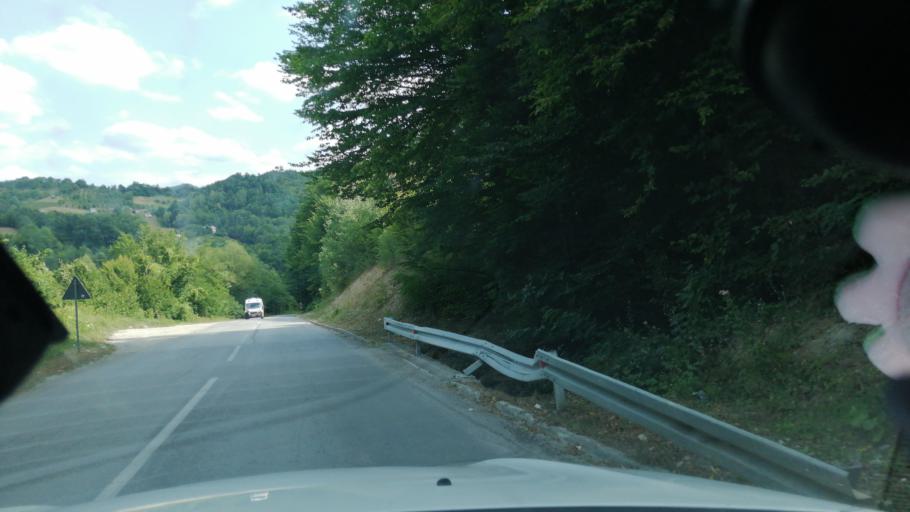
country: RS
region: Central Serbia
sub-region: Moravicki Okrug
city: Ivanjica
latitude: 43.6178
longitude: 20.2341
